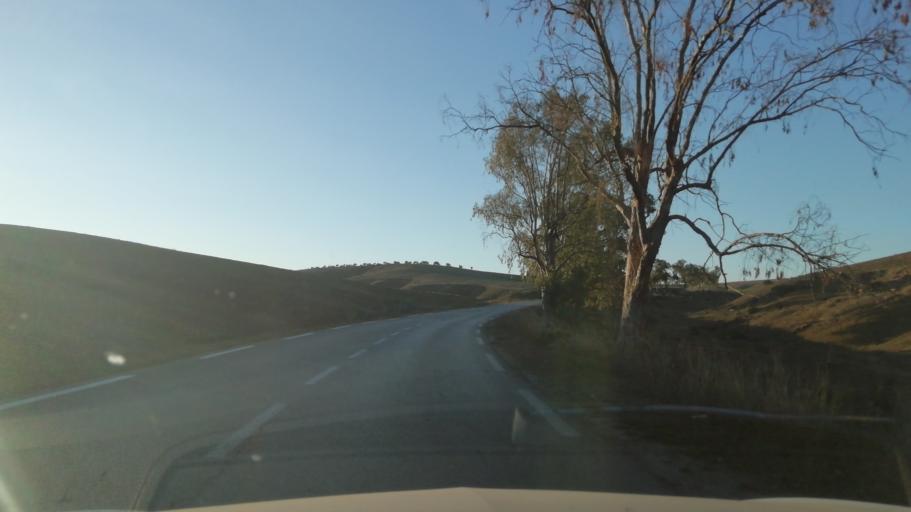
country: DZ
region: Tlemcen
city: Nedroma
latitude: 34.8281
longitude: -1.6612
